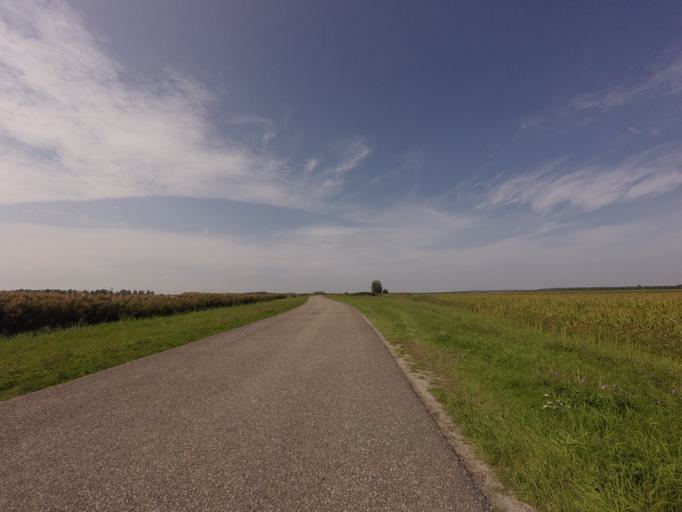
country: NL
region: Groningen
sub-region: Gemeente De Marne
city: Ulrum
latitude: 53.3461
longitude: 6.2737
